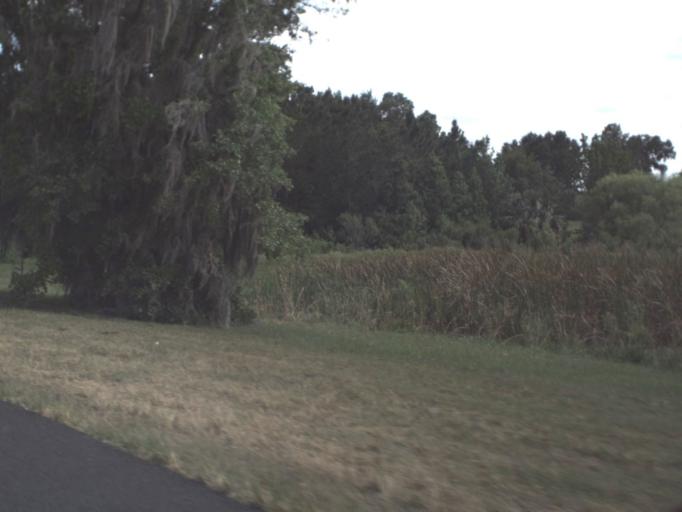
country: US
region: Florida
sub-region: Marion County
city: Ocala
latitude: 29.2491
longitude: -82.2944
